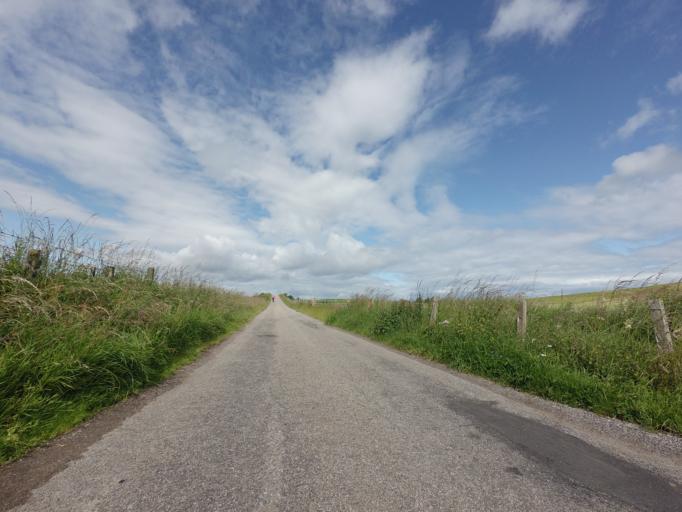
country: GB
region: Scotland
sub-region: Moray
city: Burghead
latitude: 57.6537
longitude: -3.4705
